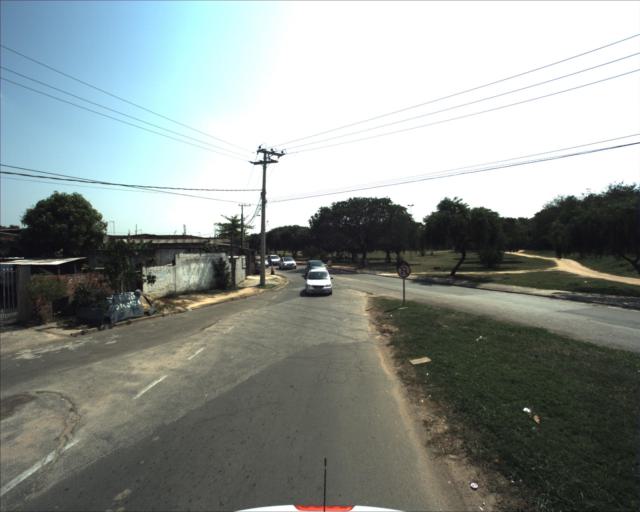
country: BR
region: Sao Paulo
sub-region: Sorocaba
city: Sorocaba
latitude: -23.4314
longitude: -47.4510
